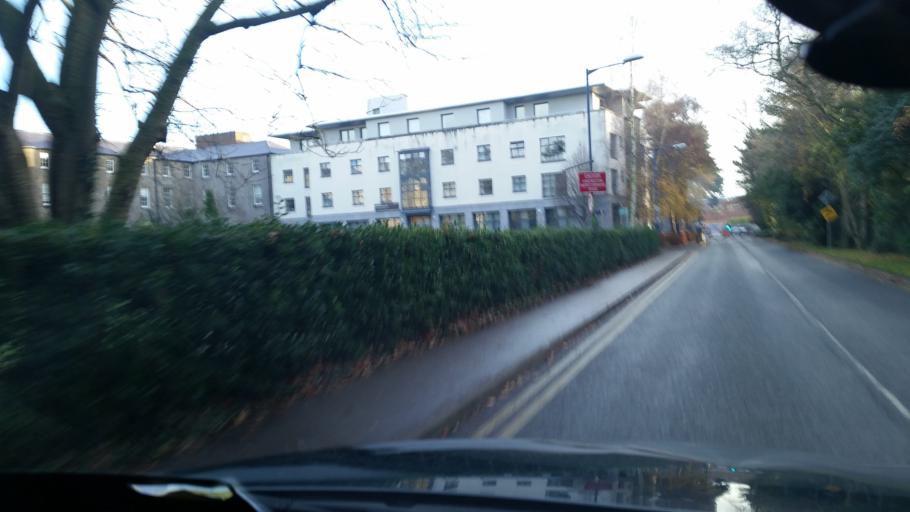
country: IE
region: Leinster
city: Glasnevin
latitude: 53.3849
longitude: -6.2615
